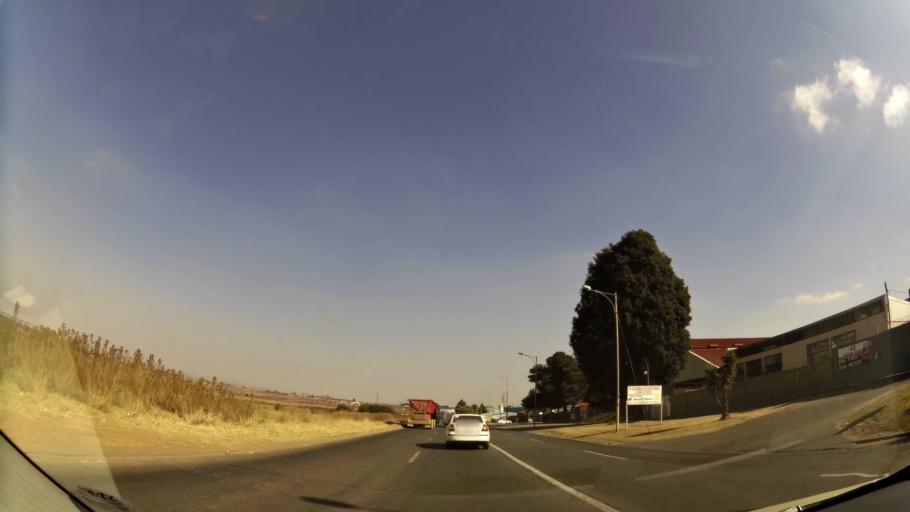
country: ZA
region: Gauteng
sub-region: City of Johannesburg Metropolitan Municipality
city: Roodepoort
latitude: -26.1488
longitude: 27.8123
